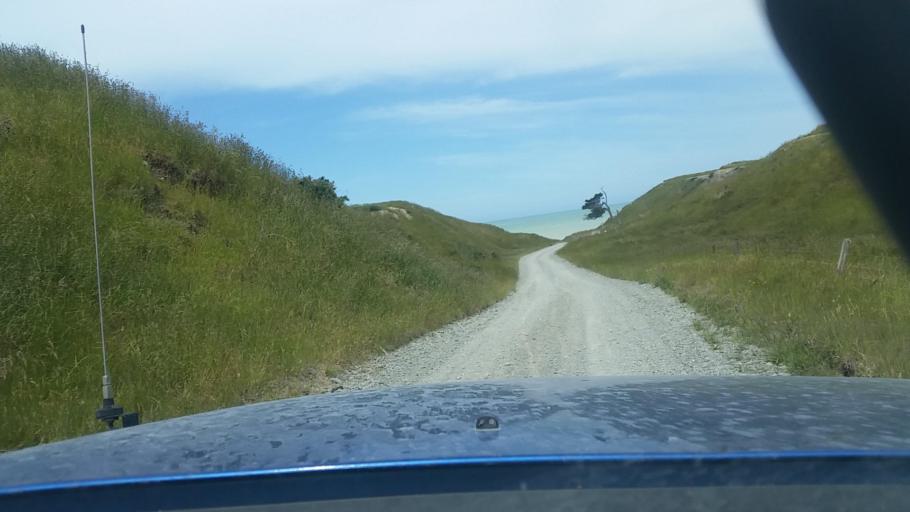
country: NZ
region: Canterbury
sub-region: Ashburton District
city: Tinwald
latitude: -44.0548
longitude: 171.7939
